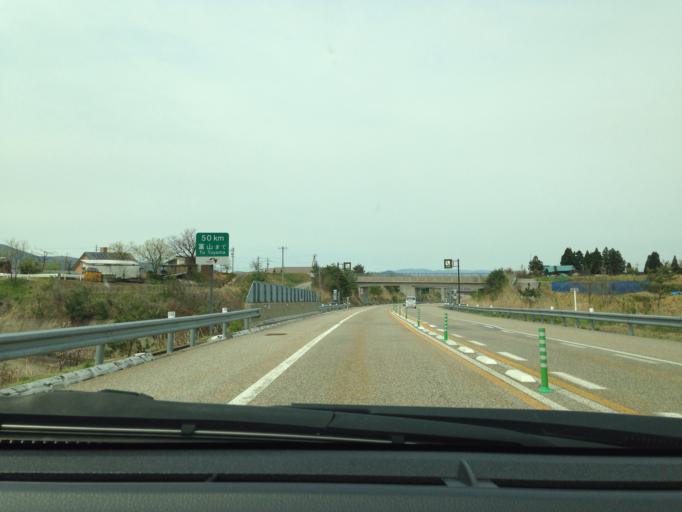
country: JP
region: Toyama
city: Fukumitsu
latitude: 36.4980
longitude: 136.8748
